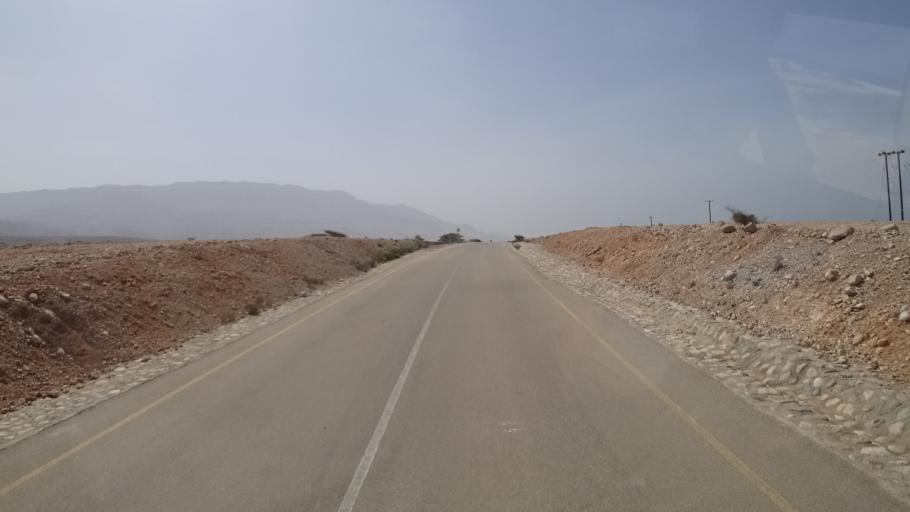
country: OM
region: Ash Sharqiyah
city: Sur
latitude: 22.9788
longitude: 59.1559
